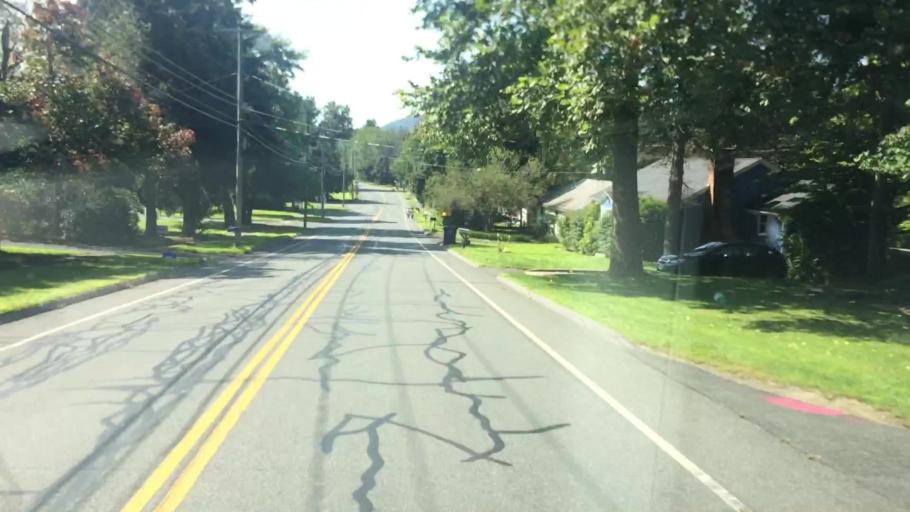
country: US
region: Massachusetts
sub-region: Hampshire County
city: South Amherst
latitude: 42.3484
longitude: -72.5201
